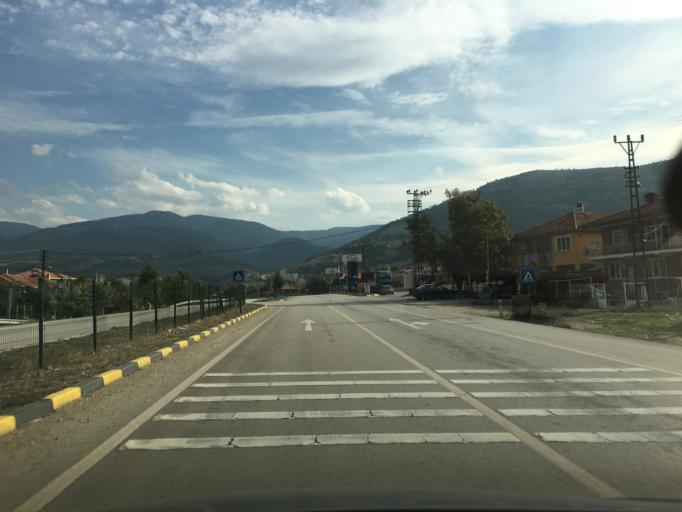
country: TR
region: Karabuk
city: Karabuk
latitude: 41.1050
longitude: 32.6689
